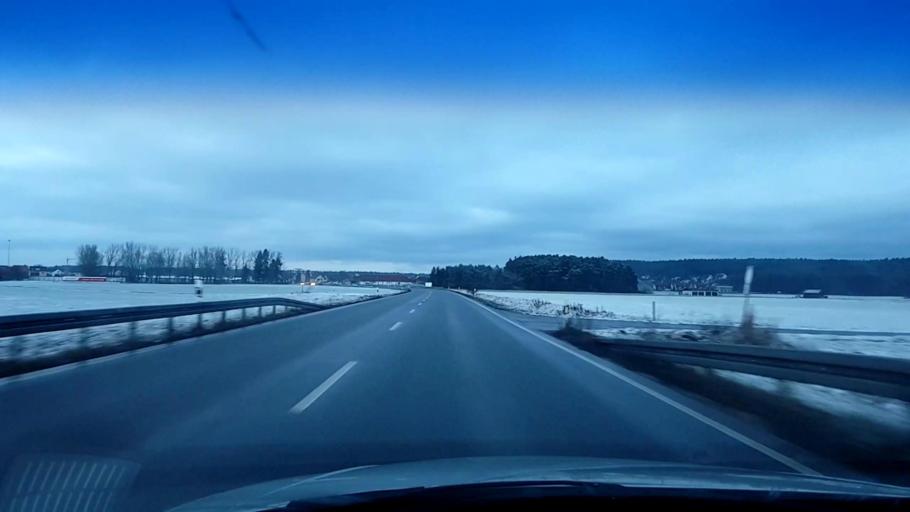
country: DE
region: Bavaria
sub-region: Upper Franconia
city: Strullendorf
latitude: 49.8357
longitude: 10.9767
